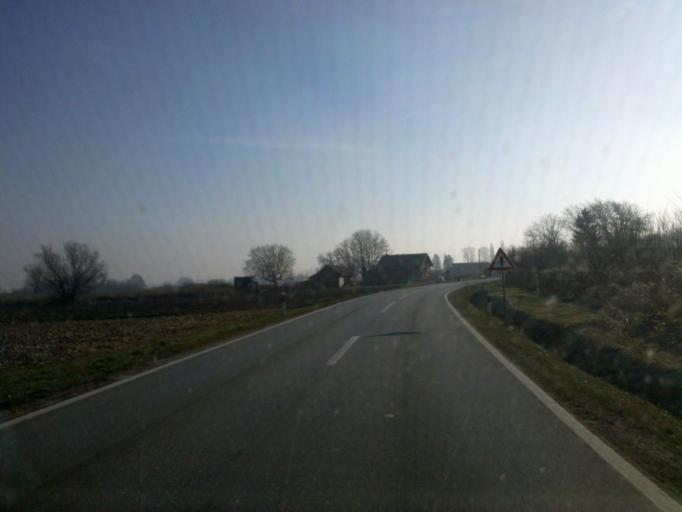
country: HR
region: Koprivnicko-Krizevacka
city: Hlebine
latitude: 46.0982
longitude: 16.9275
